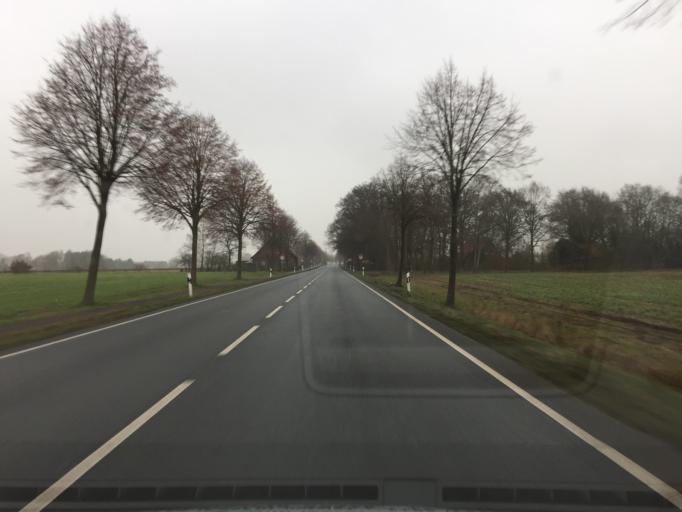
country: DE
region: Lower Saxony
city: Sulingen
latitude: 52.6608
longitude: 8.8103
